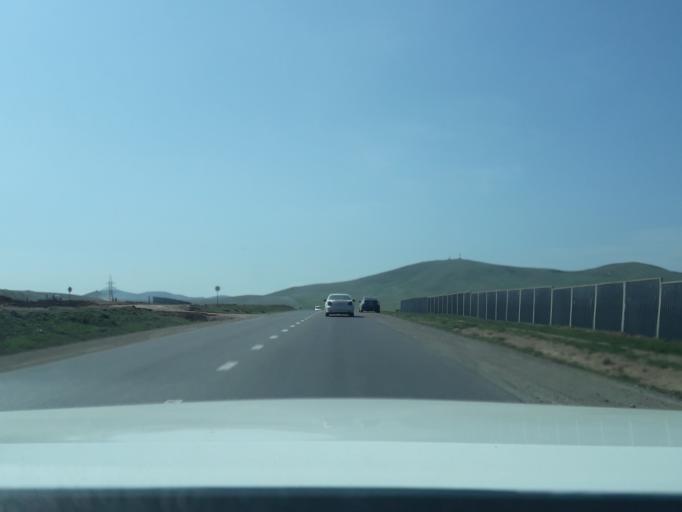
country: MN
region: Ulaanbaatar
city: Ulaanbaatar
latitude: 47.8037
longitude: 106.7484
